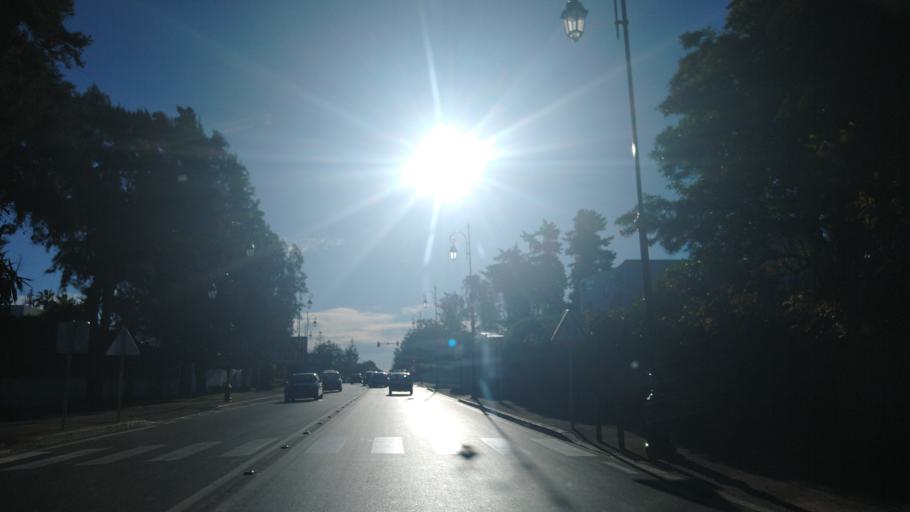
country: MA
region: Rabat-Sale-Zemmour-Zaer
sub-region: Rabat
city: Rabat
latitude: 33.9776
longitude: -6.8397
